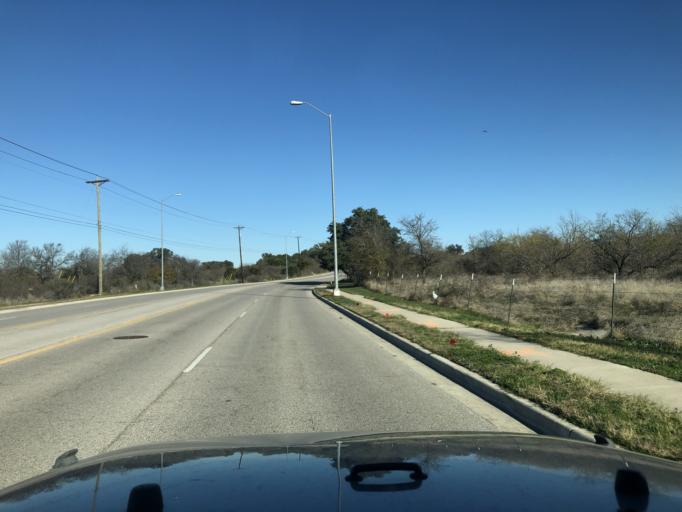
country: US
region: Texas
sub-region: Williamson County
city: Round Rock
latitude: 30.5290
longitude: -97.6949
